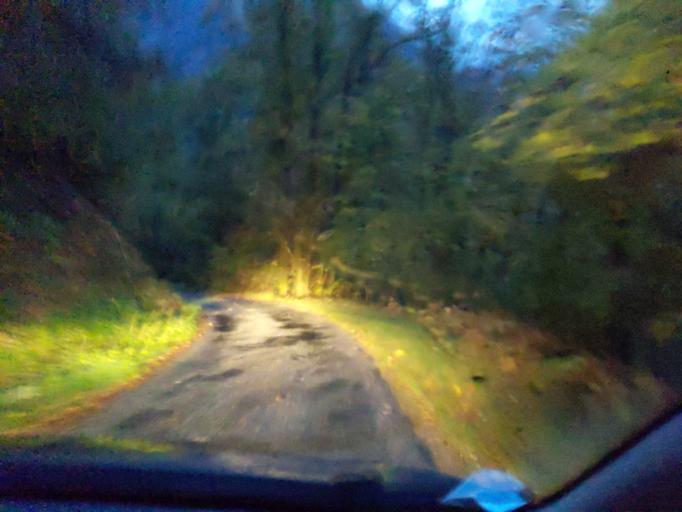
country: FR
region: Rhone-Alpes
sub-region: Departement de la Savoie
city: Aiton
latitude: 45.5200
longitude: 6.3308
